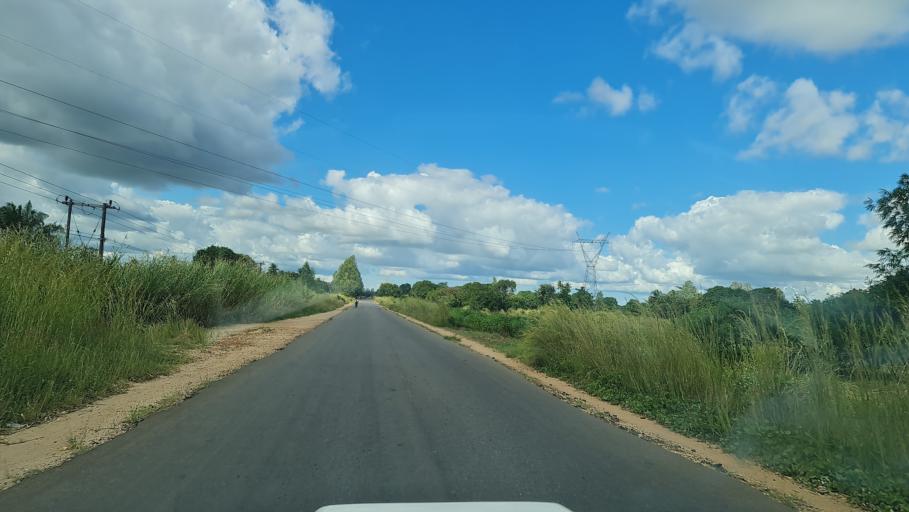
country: MZ
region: Zambezia
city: Quelimane
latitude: -17.5985
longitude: 36.7932
